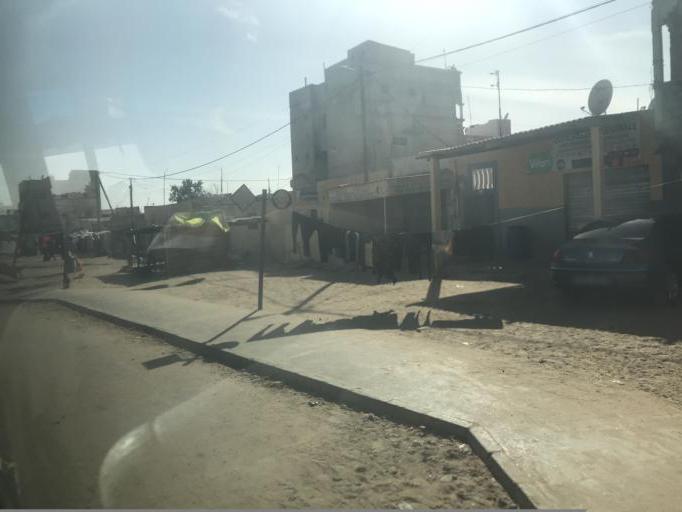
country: SN
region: Saint-Louis
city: Saint-Louis
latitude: 16.0434
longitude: -16.5054
